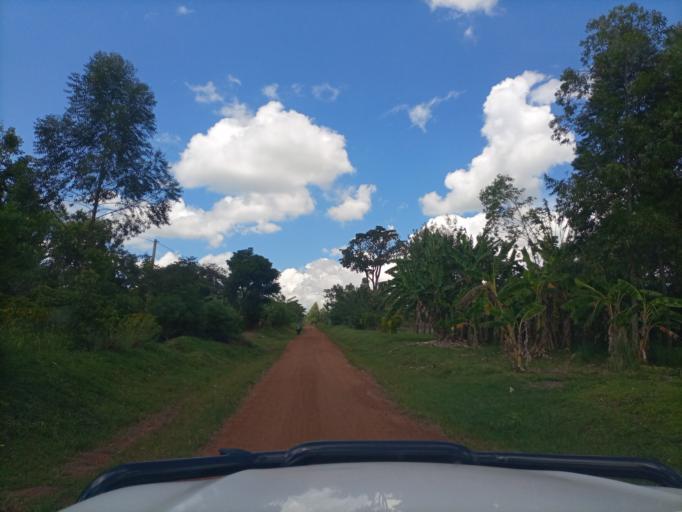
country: UG
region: Eastern Region
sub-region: Tororo District
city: Tororo
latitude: 0.7062
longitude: 34.0139
